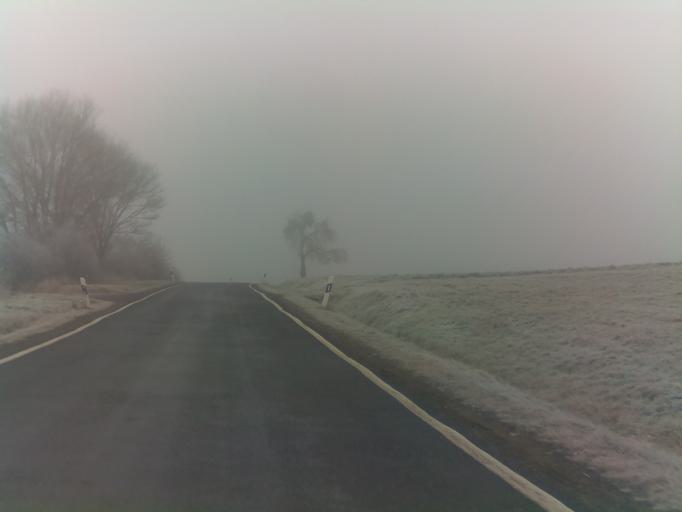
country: DE
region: Bavaria
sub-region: Regierungsbezirk Unterfranken
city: Donnersdorf
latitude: 49.9496
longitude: 10.4305
